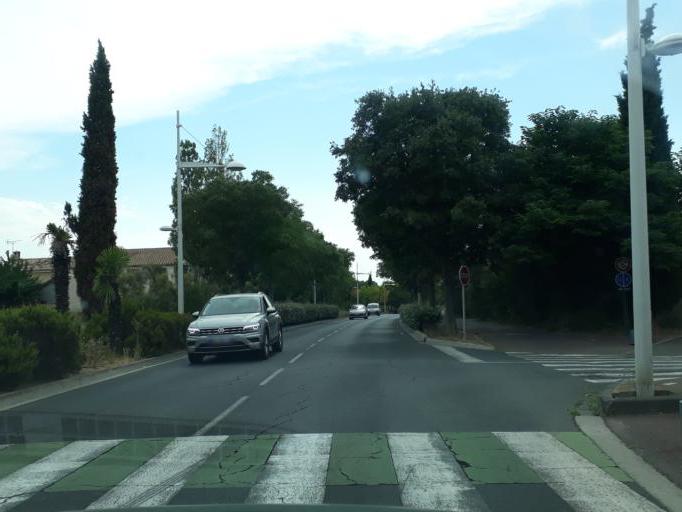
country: FR
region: Languedoc-Roussillon
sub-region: Departement de l'Herault
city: Agde
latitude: 43.3070
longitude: 3.4721
